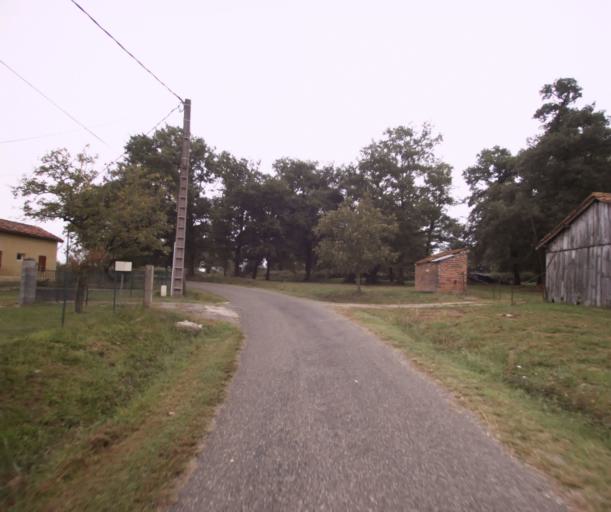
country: FR
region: Midi-Pyrenees
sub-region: Departement du Gers
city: Cazaubon
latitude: 43.9208
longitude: -0.1863
